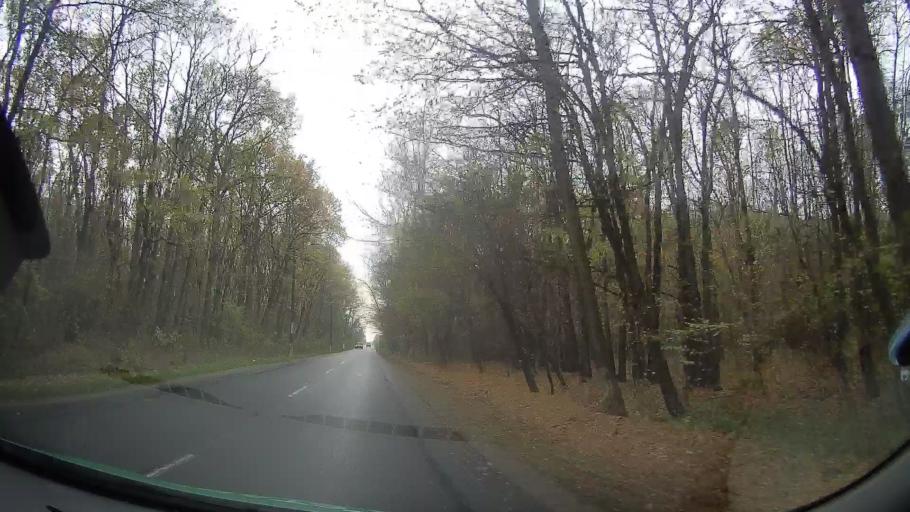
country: RO
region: Ilfov
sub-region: Comuna Snagov
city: Snagov
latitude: 44.7153
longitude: 26.1957
